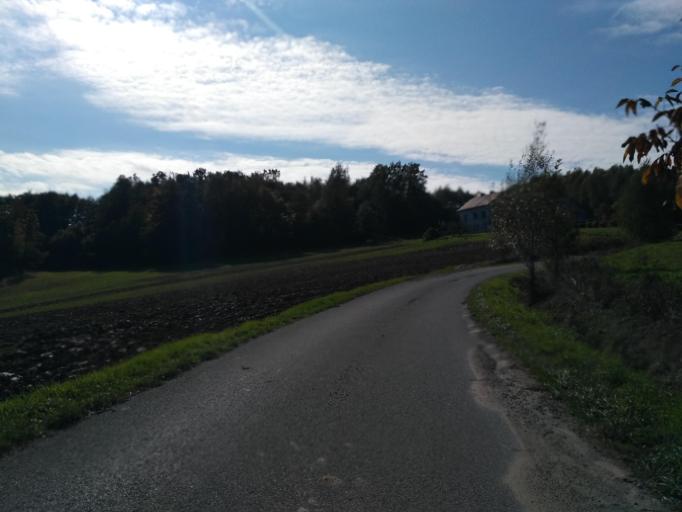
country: PL
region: Subcarpathian Voivodeship
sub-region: Powiat debicki
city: Slotowa
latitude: 49.9345
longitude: 21.2761
